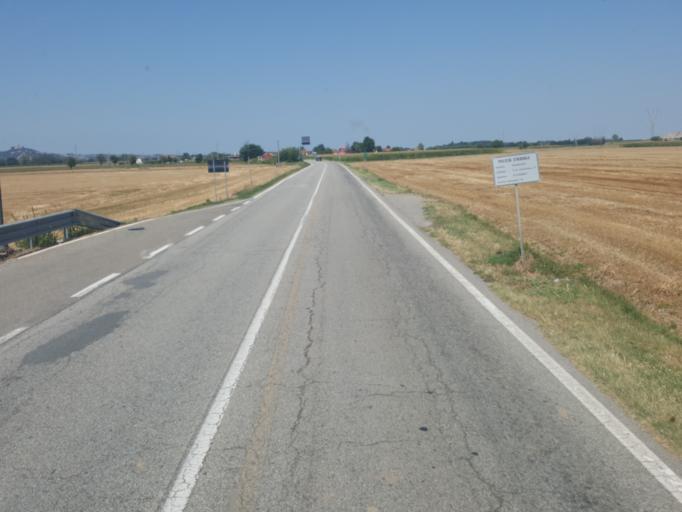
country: IT
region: Piedmont
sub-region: Provincia di Alessandria
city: Spinetta Marengo
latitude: 44.8947
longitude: 8.6764
